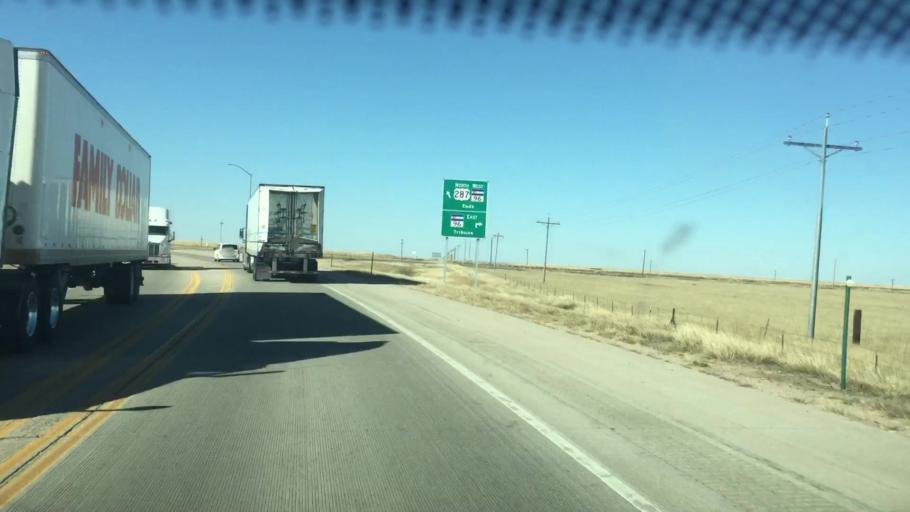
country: US
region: Colorado
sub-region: Kiowa County
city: Eads
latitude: 38.4704
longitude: -102.7308
